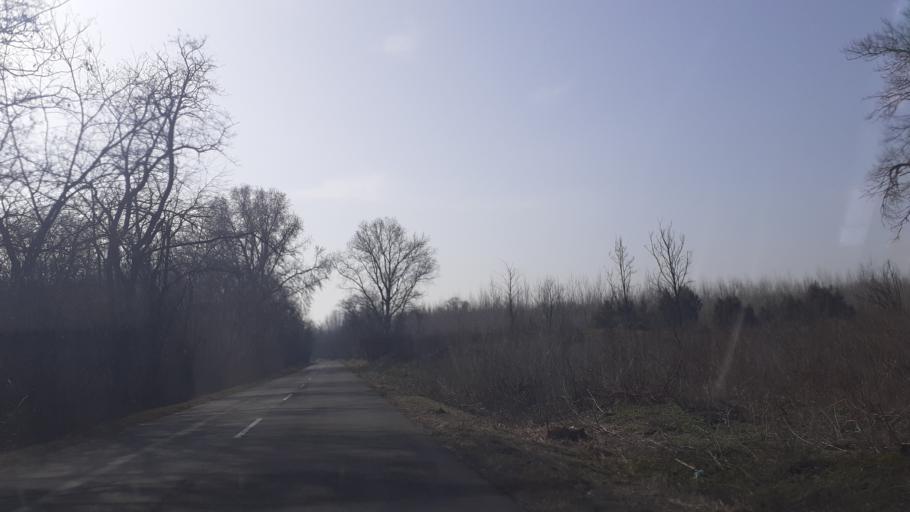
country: HU
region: Pest
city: Orkeny
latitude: 47.0972
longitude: 19.3866
